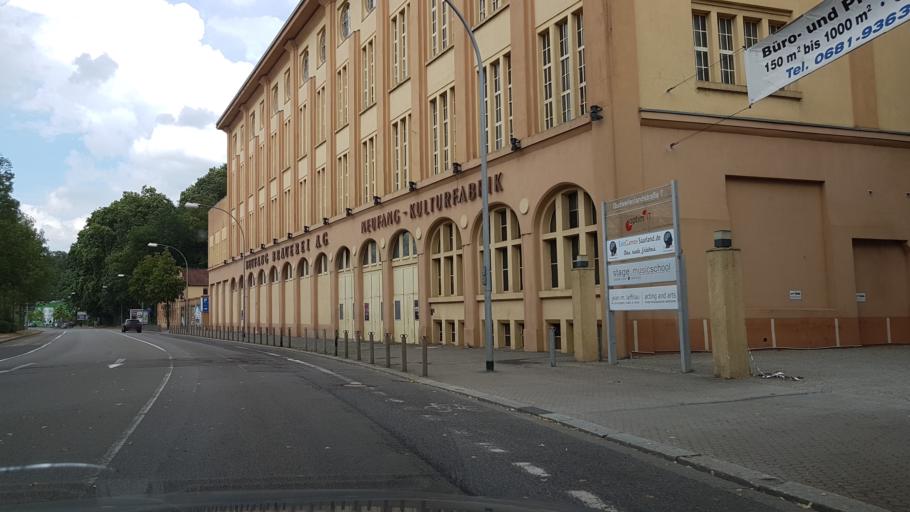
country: DE
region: Saarland
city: Saarbrucken
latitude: 49.2435
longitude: 7.0035
